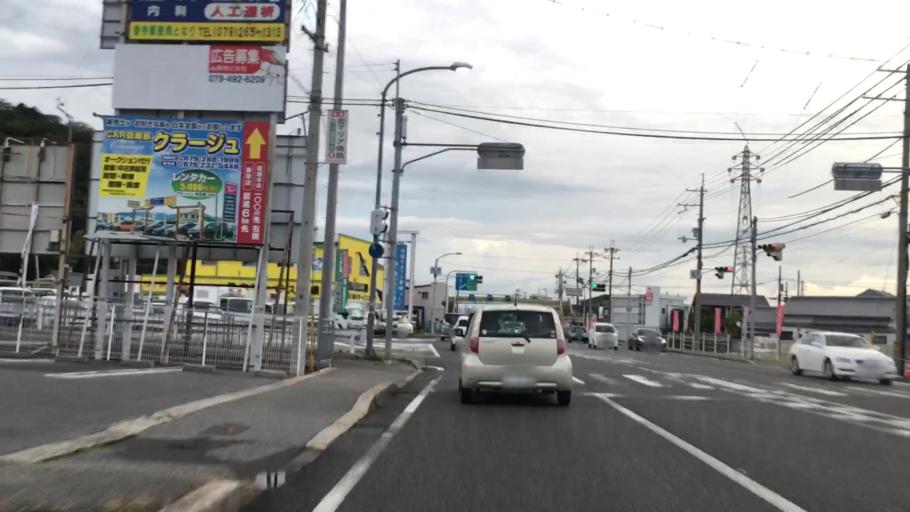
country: JP
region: Hyogo
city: Himeji
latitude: 34.8705
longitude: 134.7292
